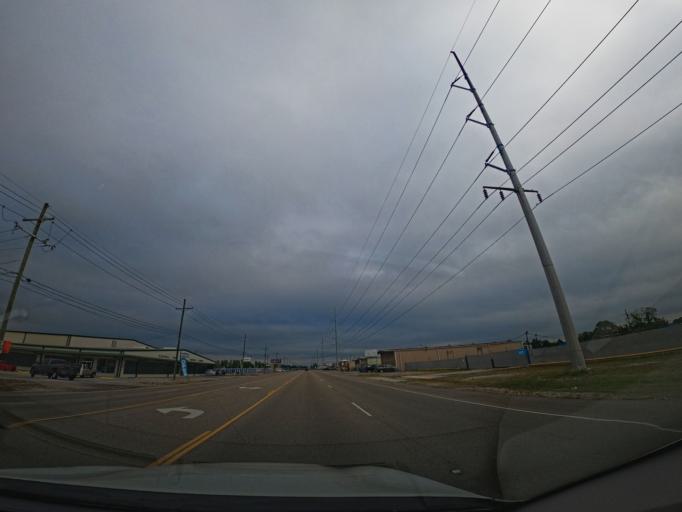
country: US
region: Louisiana
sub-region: Terrebonne Parish
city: Presquille
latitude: 29.5620
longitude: -90.6814
